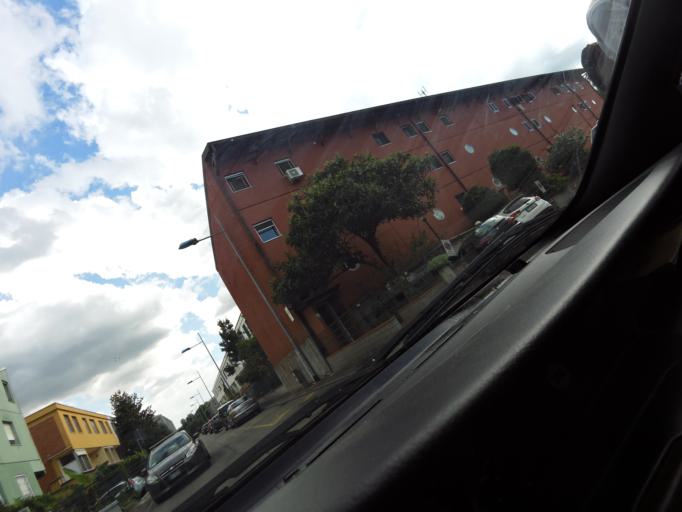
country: IT
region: Lombardy
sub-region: Citta metropolitana di Milano
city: Poasco-Sorigherio
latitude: 45.4037
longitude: 9.2310
